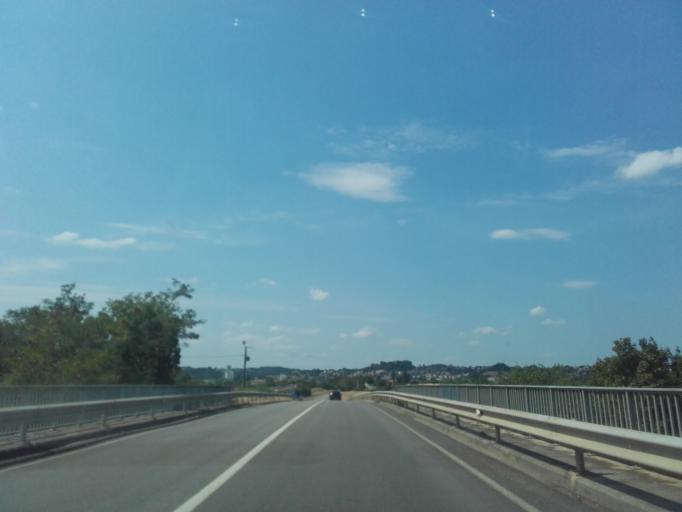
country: FR
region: Rhone-Alpes
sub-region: Departement de l'Ain
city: Meximieux
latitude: 45.8862
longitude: 5.2124
